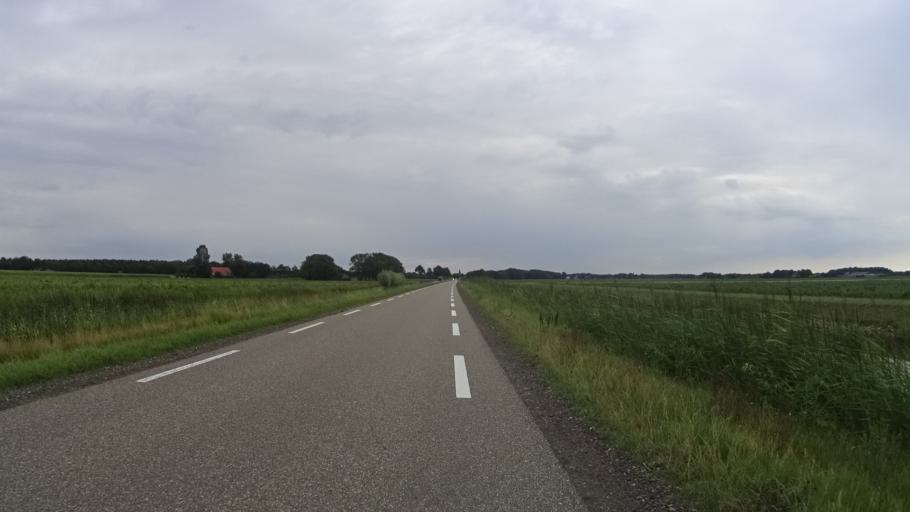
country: NL
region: Groningen
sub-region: Gemeente Slochteren
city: Slochteren
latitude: 53.2275
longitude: 6.7754
